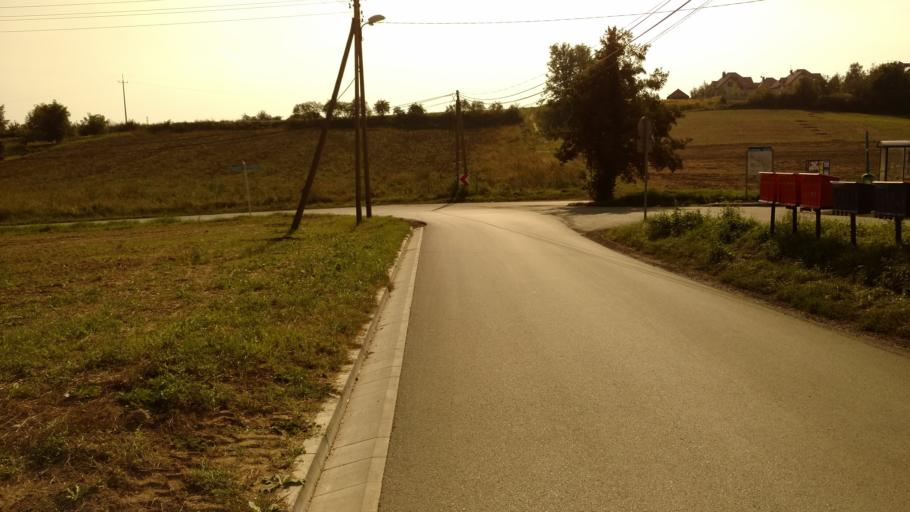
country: PL
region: Lesser Poland Voivodeship
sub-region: Powiat krakowski
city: Michalowice
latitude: 50.1287
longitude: 19.9836
